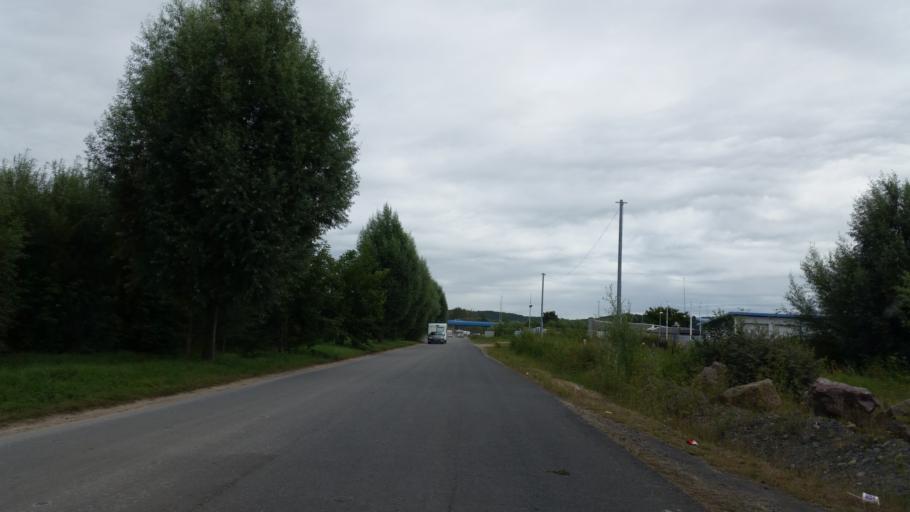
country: FR
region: Lower Normandy
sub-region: Departement du Calvados
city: La Riviere-Saint-Sauveur
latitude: 49.4194
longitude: 0.2710
